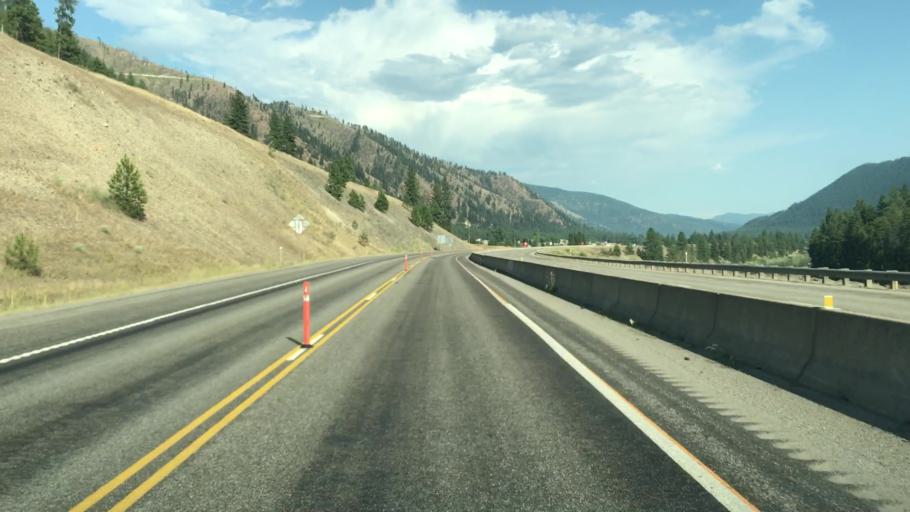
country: US
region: Montana
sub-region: Mineral County
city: Superior
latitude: 47.2168
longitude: -114.9513
